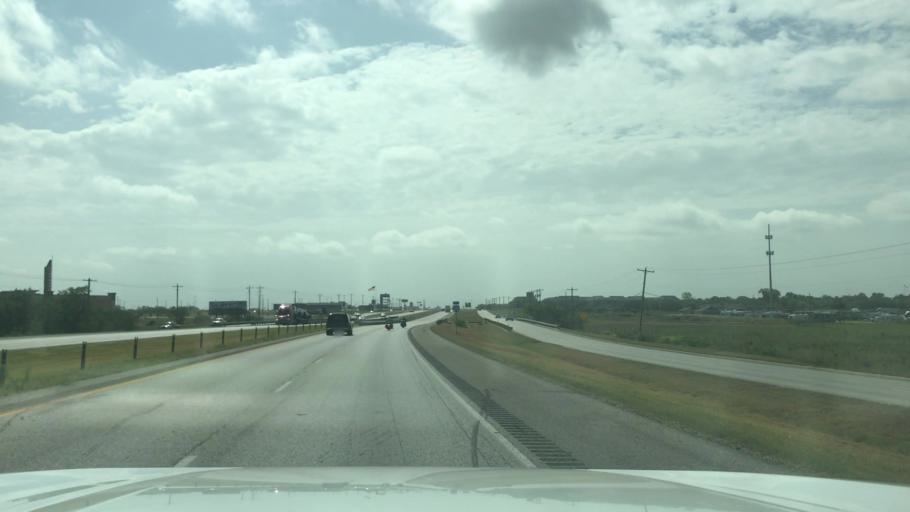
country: US
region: Texas
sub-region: Taylor County
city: Abilene
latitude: 32.4881
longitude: -99.7166
